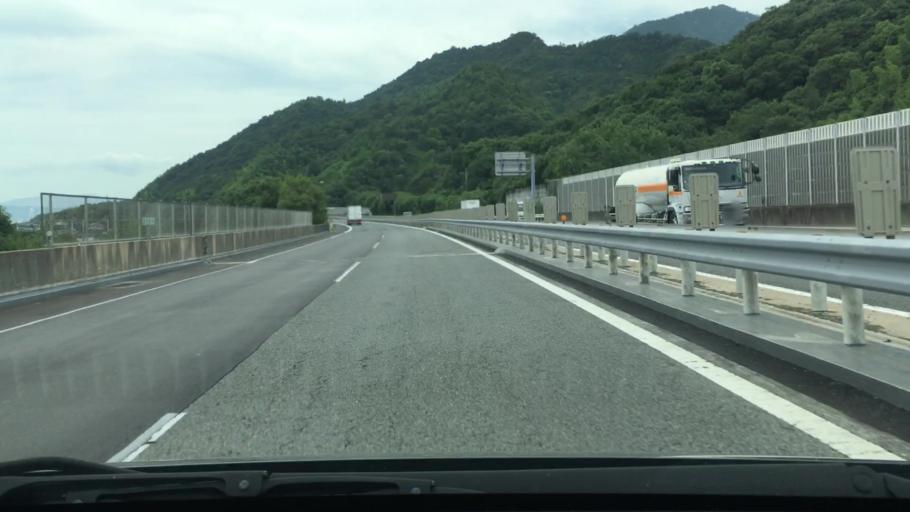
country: JP
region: Hiroshima
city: Ono-hara
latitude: 34.2990
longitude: 132.2722
